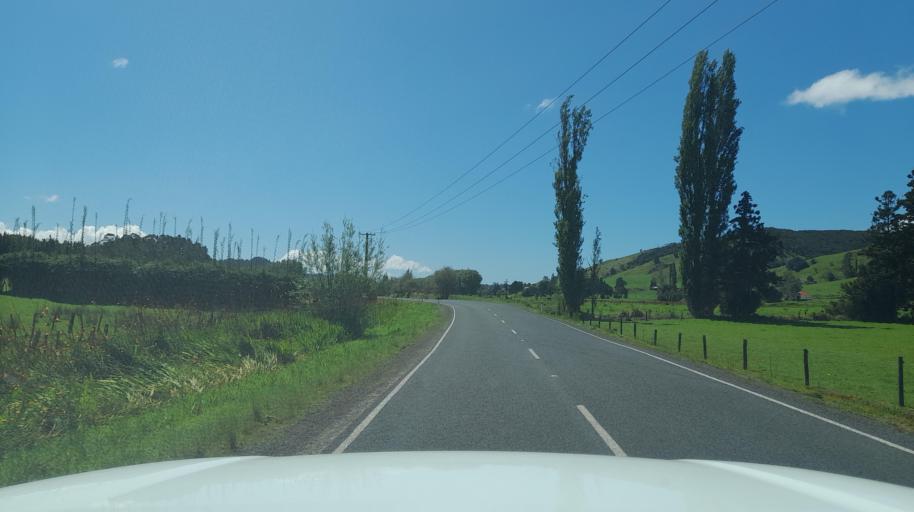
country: NZ
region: Northland
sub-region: Far North District
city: Taipa
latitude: -35.0772
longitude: 173.5086
